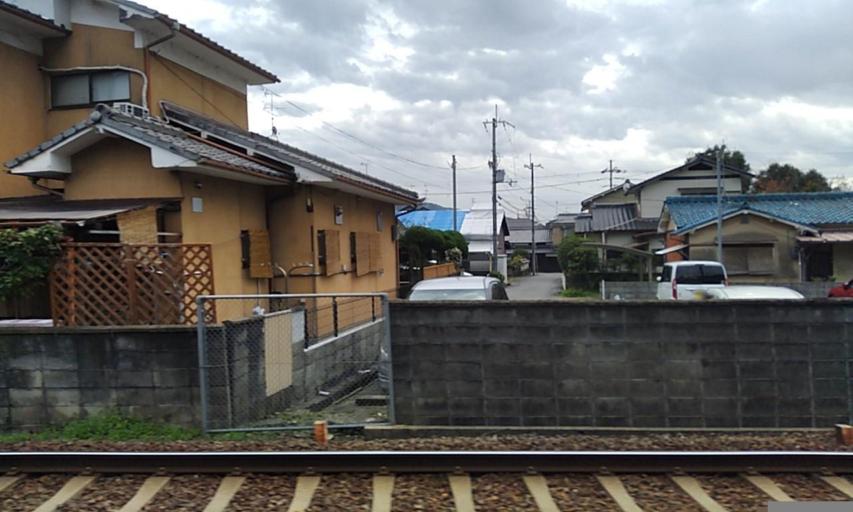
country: JP
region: Shiga Prefecture
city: Otsu-shi
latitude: 34.9922
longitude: 135.8264
